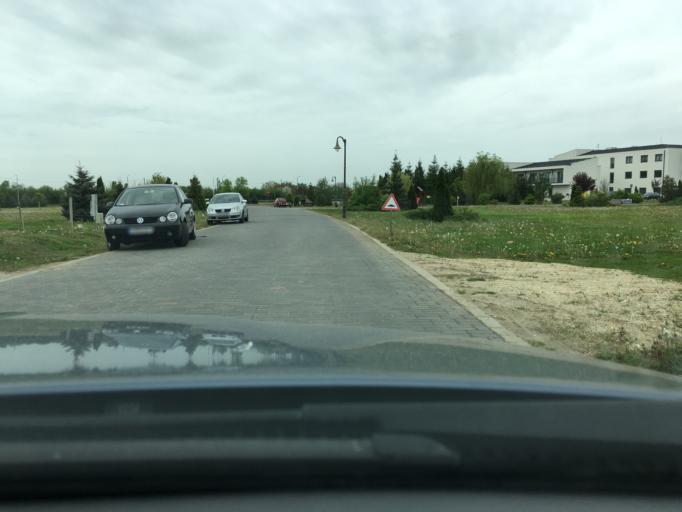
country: HU
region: Hajdu-Bihar
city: Debrecen
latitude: 47.5499
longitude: 21.6891
